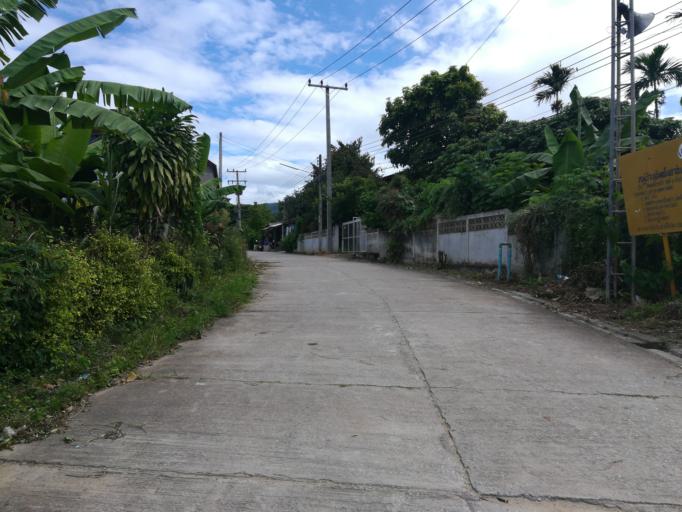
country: TH
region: Chiang Mai
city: Chom Thong
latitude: 18.4072
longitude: 98.6496
